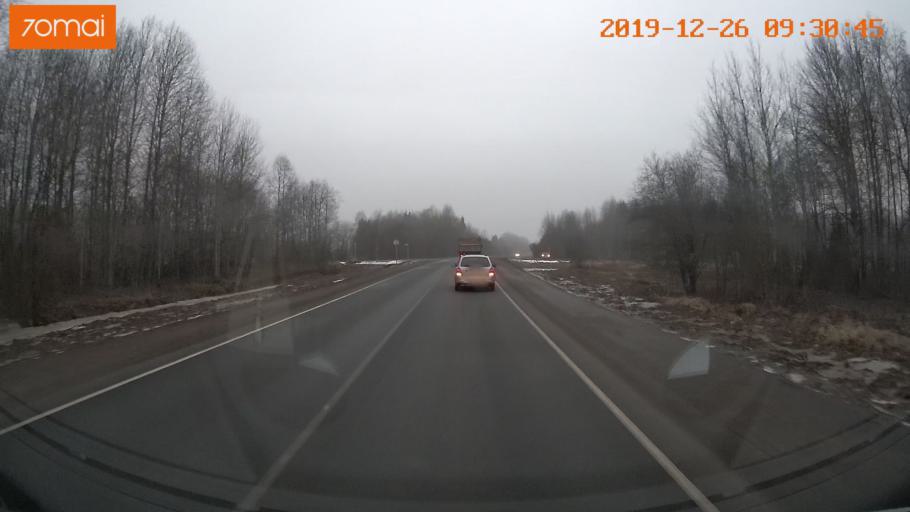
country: RU
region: Vologda
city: Gryazovets
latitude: 59.0632
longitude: 40.1362
